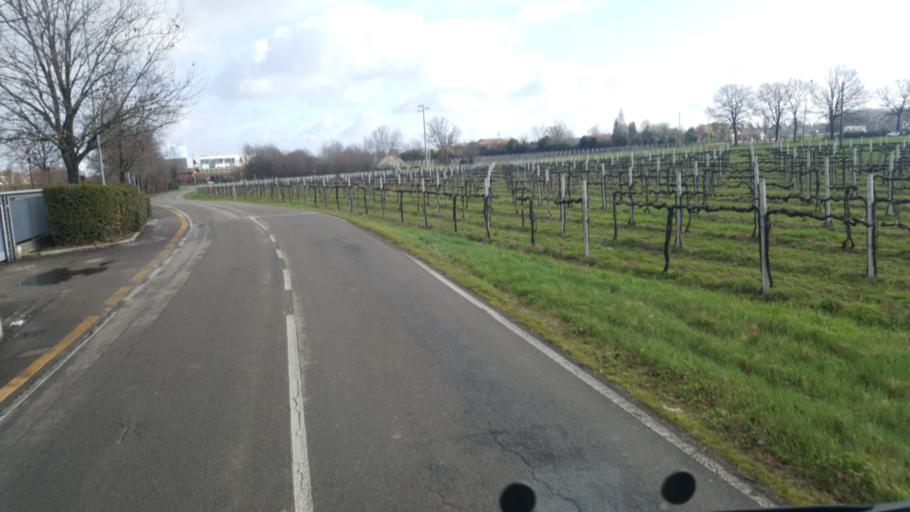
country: IT
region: Emilia-Romagna
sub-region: Provincia di Reggio Emilia
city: Fellegara
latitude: 44.6110
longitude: 10.7016
